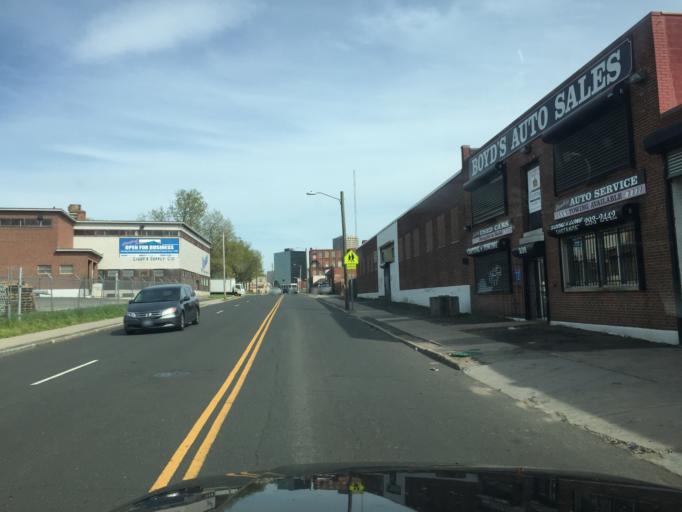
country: US
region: Connecticut
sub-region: Hartford County
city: Hartford
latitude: 41.7745
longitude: -72.6853
